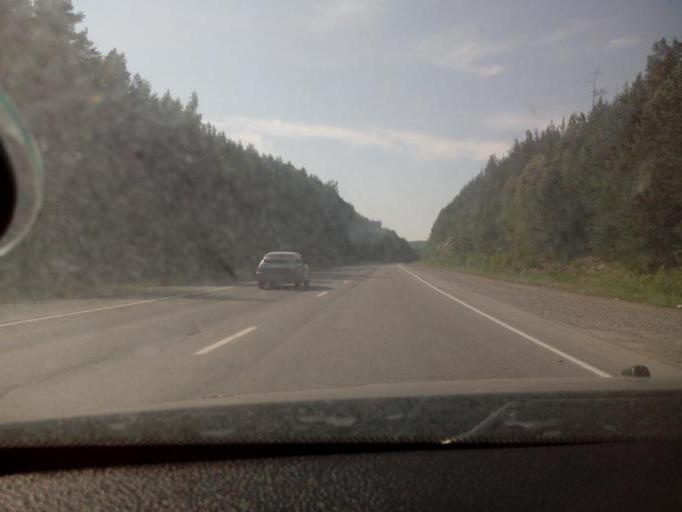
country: RU
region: Sverdlovsk
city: Sredneuralsk
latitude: 57.0677
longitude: 60.4201
